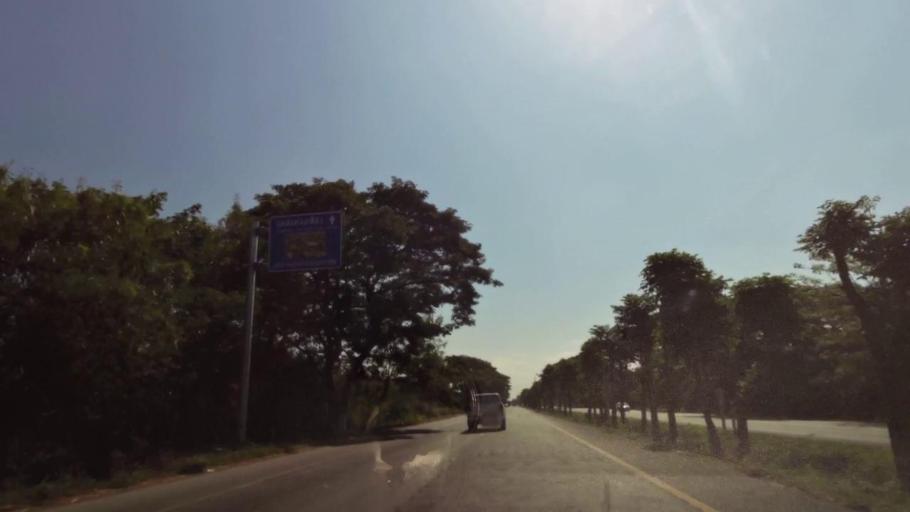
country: TH
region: Nakhon Sawan
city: Kao Liao
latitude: 15.7871
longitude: 100.1210
